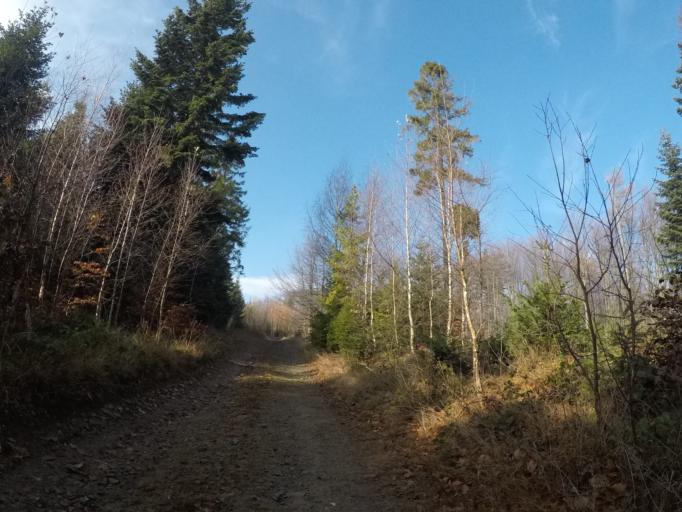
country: SK
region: Kosicky
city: Gelnica
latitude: 48.7650
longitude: 21.0633
